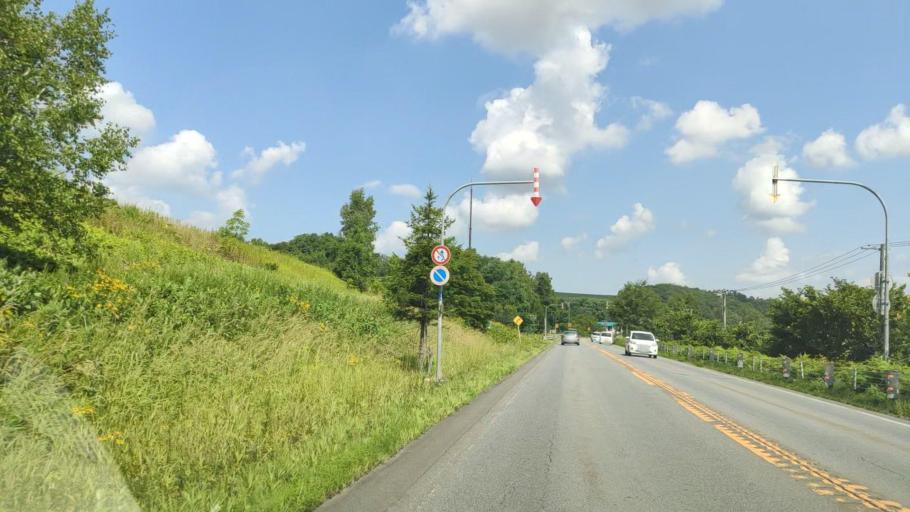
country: JP
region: Hokkaido
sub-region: Asahikawa-shi
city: Asahikawa
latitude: 43.5633
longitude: 142.4348
